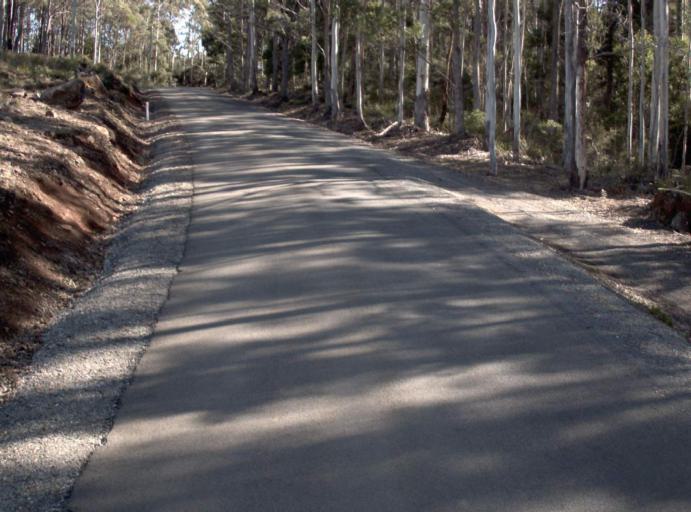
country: AU
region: Tasmania
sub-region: Launceston
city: Mayfield
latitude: -41.3191
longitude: 147.2123
